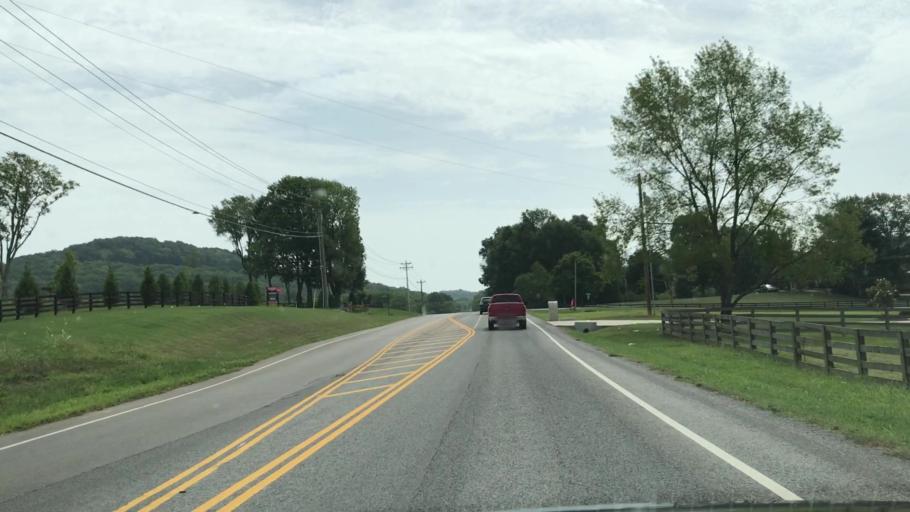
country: US
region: Tennessee
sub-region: Williamson County
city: Nolensville
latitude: 35.9278
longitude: -86.7449
